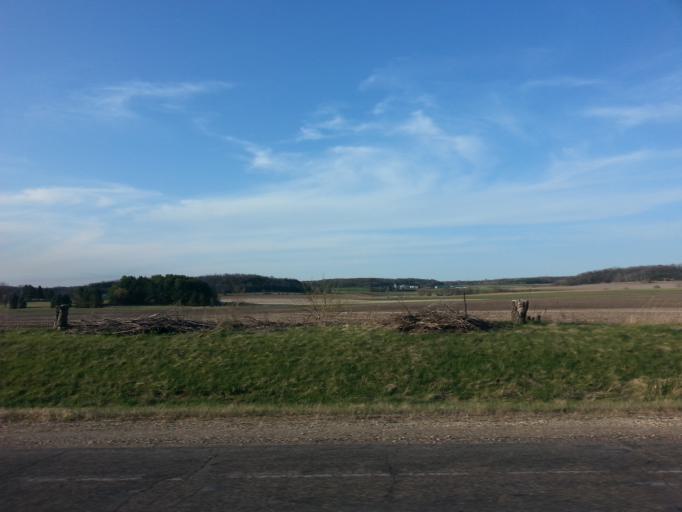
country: US
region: Wisconsin
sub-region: Pierce County
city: River Falls
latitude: 44.8627
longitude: -92.6694
